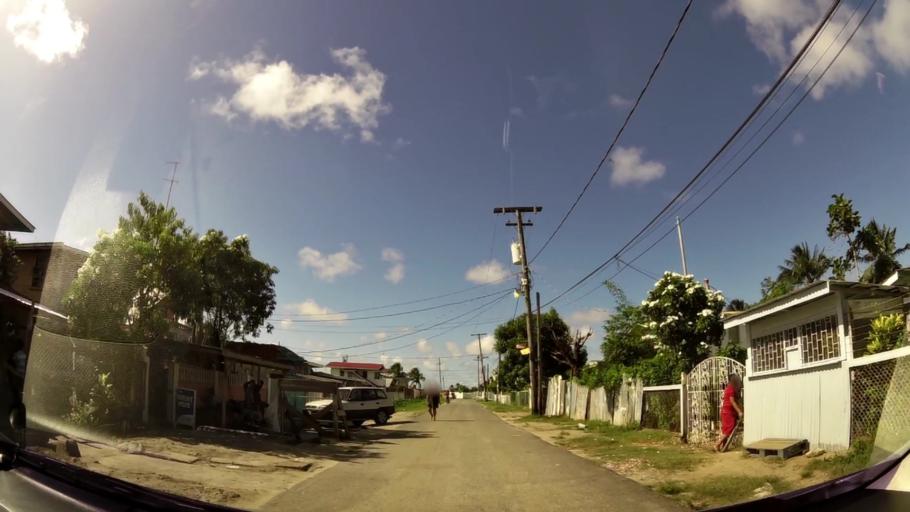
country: GY
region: Demerara-Mahaica
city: Georgetown
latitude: 6.8194
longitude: -58.1252
